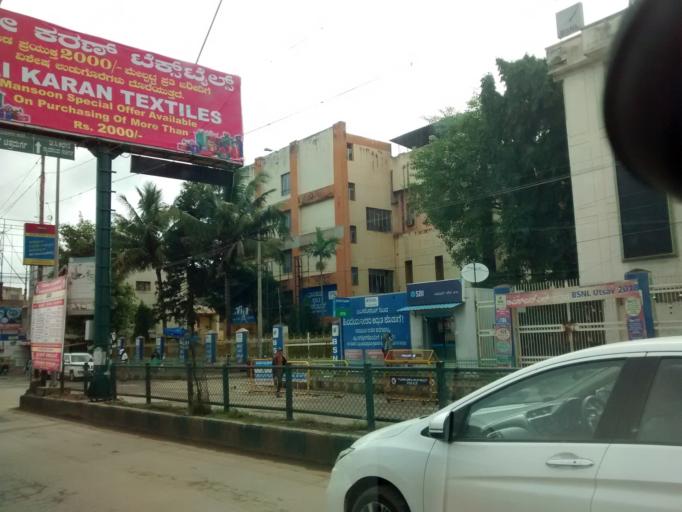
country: IN
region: Karnataka
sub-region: Tumkur
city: Tumkur
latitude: 13.3420
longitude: 77.1018
